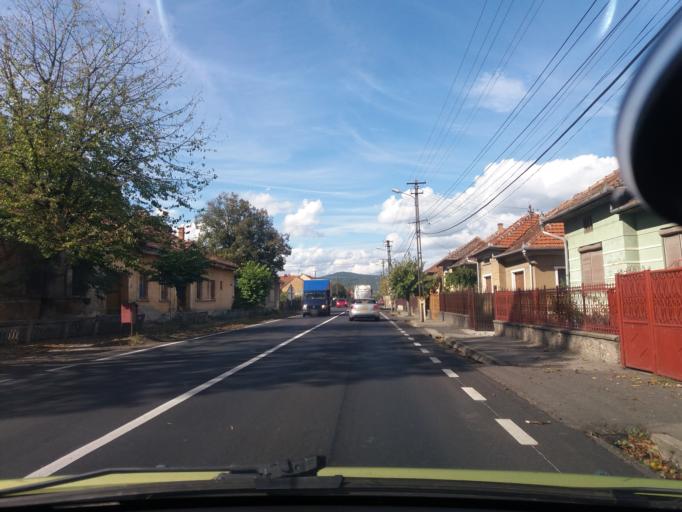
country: RO
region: Hunedoara
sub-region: Comuna Ilia
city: Ilia
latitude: 45.9349
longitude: 22.6518
